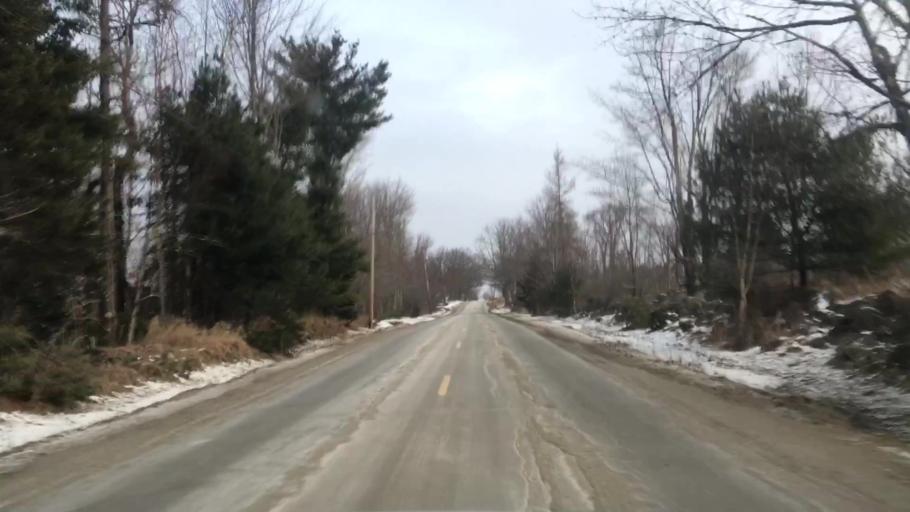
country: US
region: Maine
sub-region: Hancock County
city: Franklin
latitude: 44.7054
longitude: -68.3407
